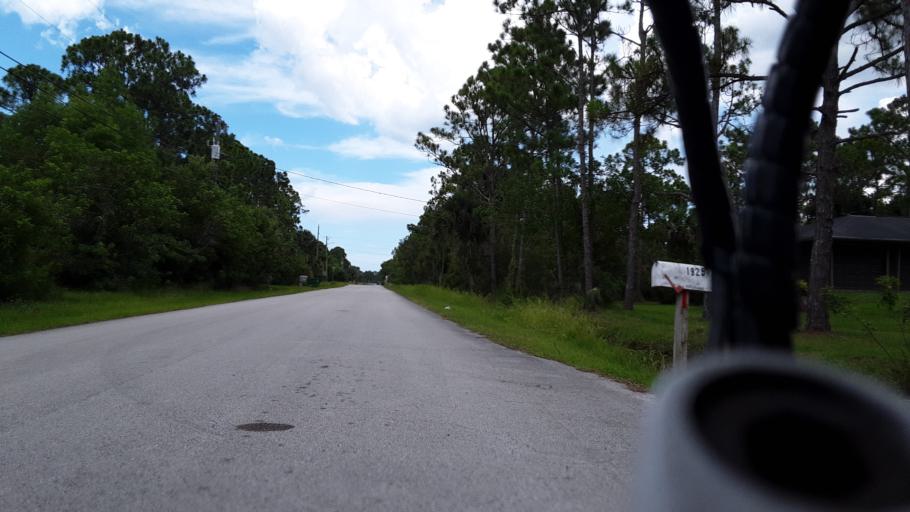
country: US
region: Florida
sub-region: Brevard County
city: Malabar
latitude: 27.9834
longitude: -80.5831
